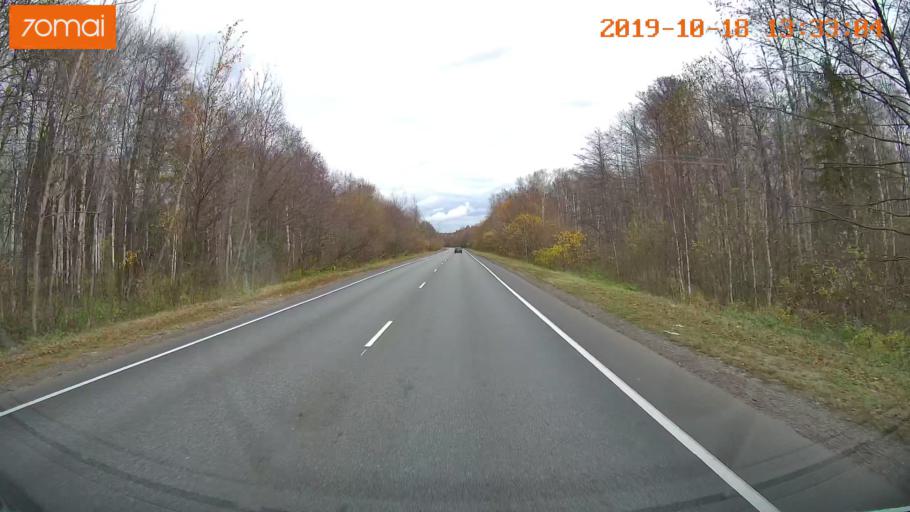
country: RU
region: Rjazan
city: Solotcha
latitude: 54.8393
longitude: 39.9286
